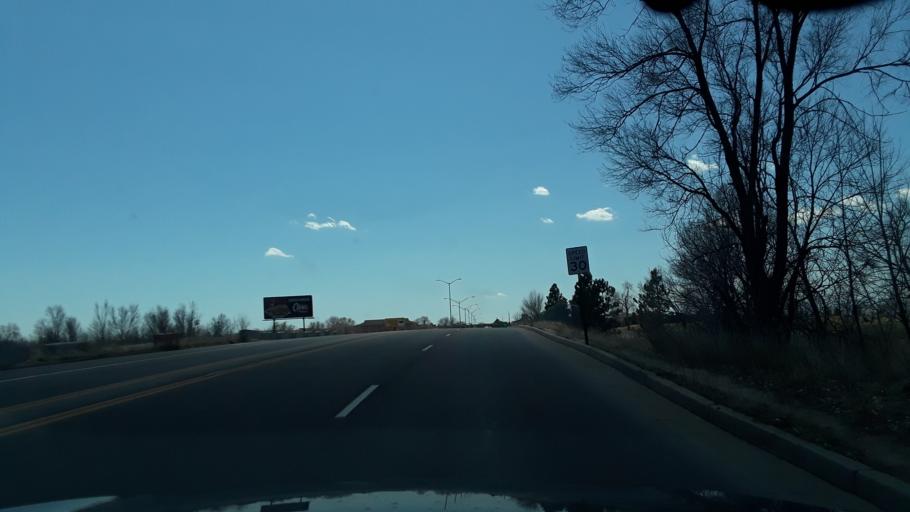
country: US
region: Colorado
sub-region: El Paso County
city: Cimarron Hills
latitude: 38.8441
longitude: -104.7015
